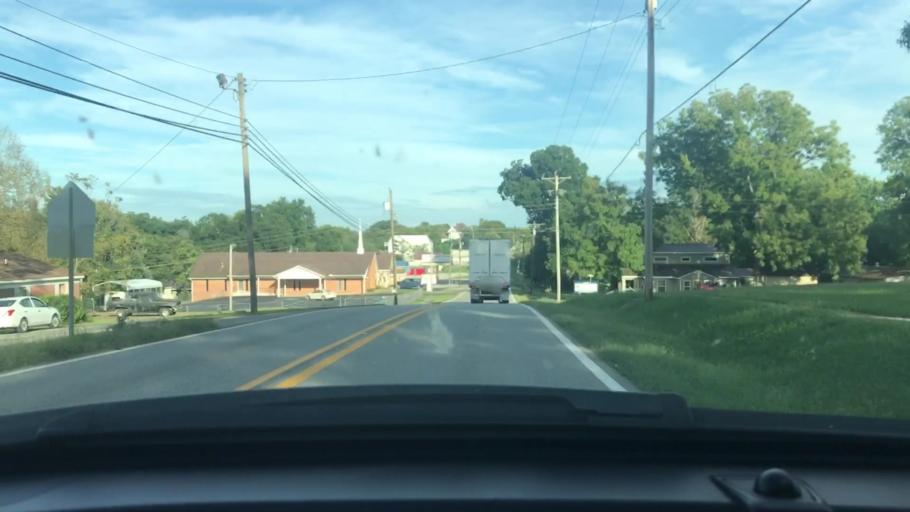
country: US
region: Arkansas
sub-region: Randolph County
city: Pocahontas
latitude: 36.2037
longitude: -91.1790
